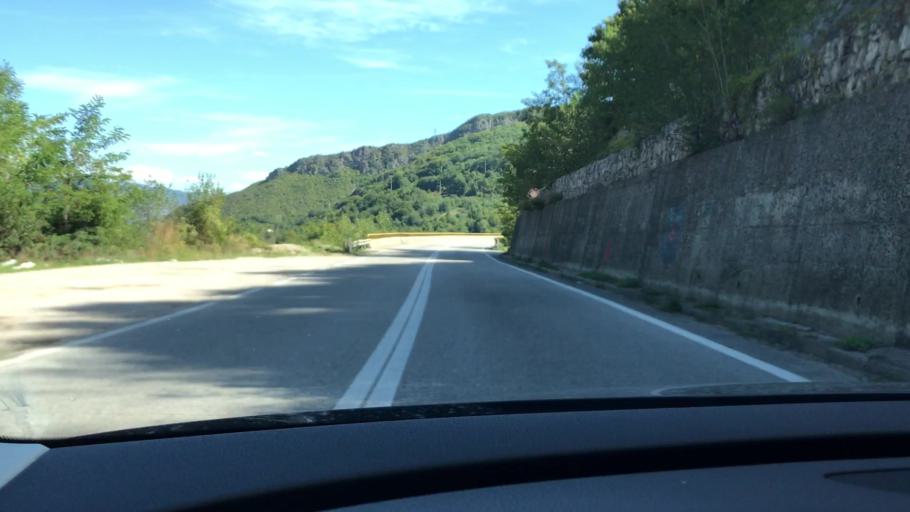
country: BA
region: Federation of Bosnia and Herzegovina
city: Jablanica
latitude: 43.6838
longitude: 17.7955
